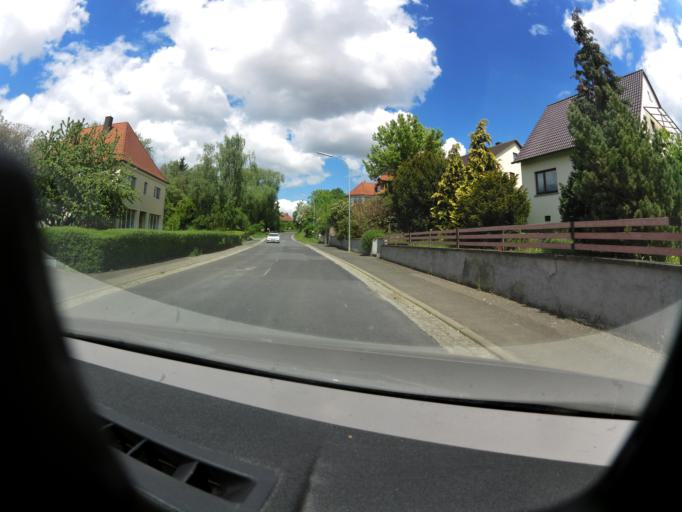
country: DE
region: Bavaria
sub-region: Regierungsbezirk Unterfranken
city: Schwanfeld
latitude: 49.9245
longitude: 10.1375
